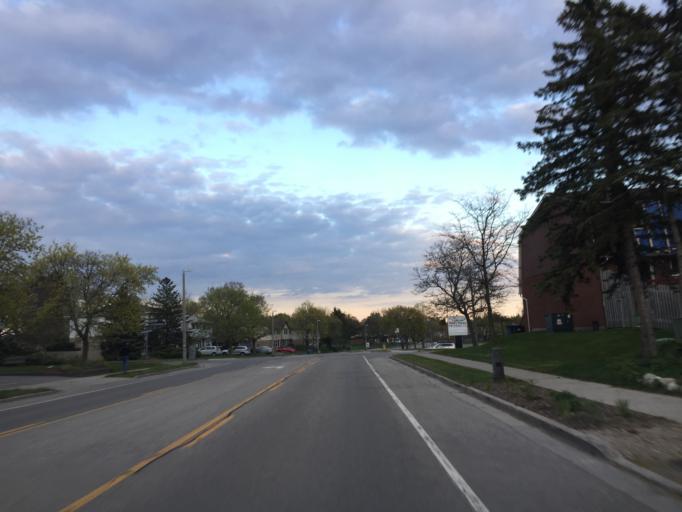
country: CA
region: Ontario
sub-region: Wellington County
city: Guelph
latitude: 43.5126
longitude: -80.2548
